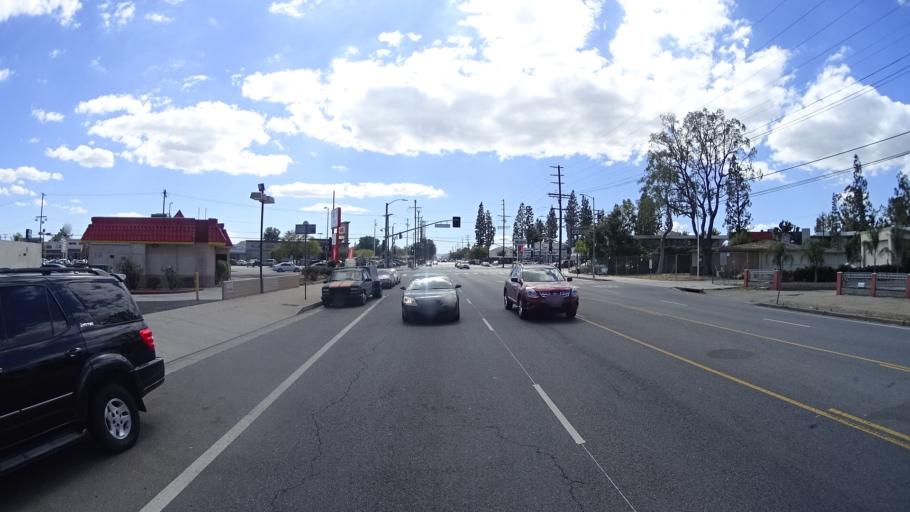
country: US
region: California
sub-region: Los Angeles County
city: San Fernando
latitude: 34.2353
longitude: -118.4394
